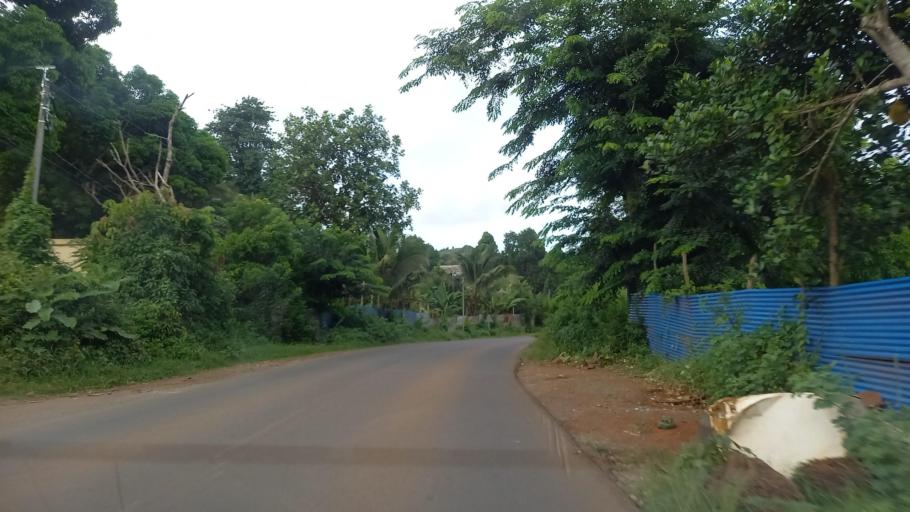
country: YT
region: Bandraboua
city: Bandraboua
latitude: -12.7287
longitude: 45.1201
